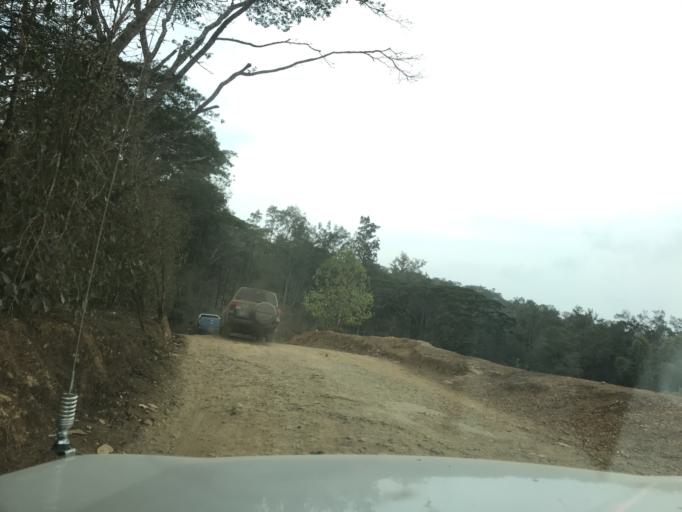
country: TL
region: Ermera
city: Gleno
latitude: -8.8337
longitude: 125.4508
